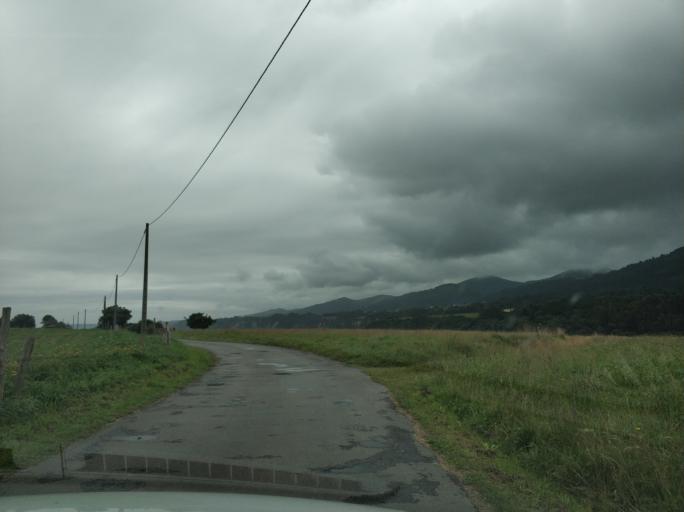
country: ES
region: Asturias
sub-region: Province of Asturias
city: Salas
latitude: 43.5536
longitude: -6.3769
